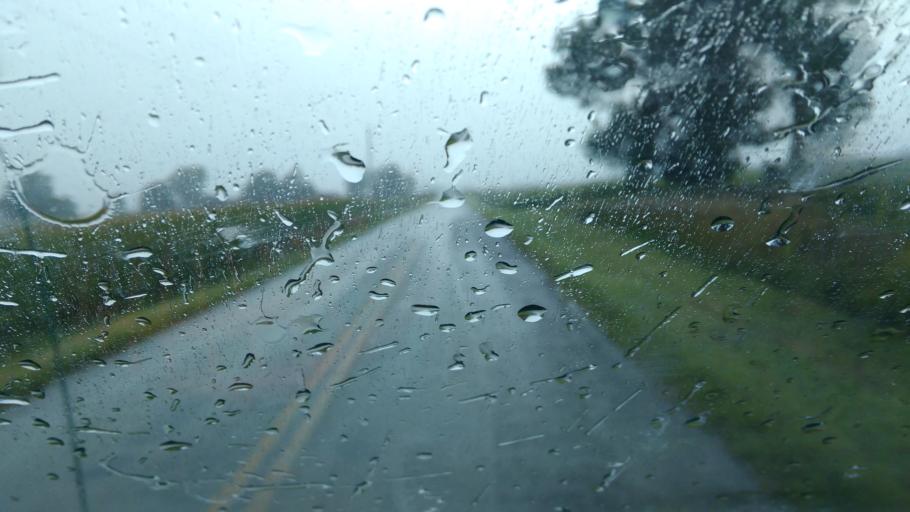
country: US
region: Ohio
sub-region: Hardin County
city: Kenton
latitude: 40.6880
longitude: -83.5379
